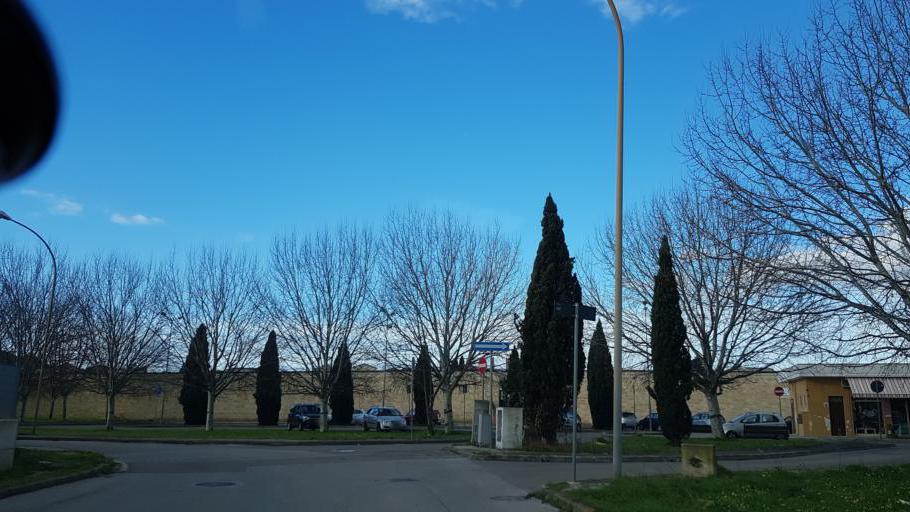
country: IT
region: Apulia
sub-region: Provincia di Brindisi
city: Brindisi
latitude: 40.6273
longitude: 17.9536
